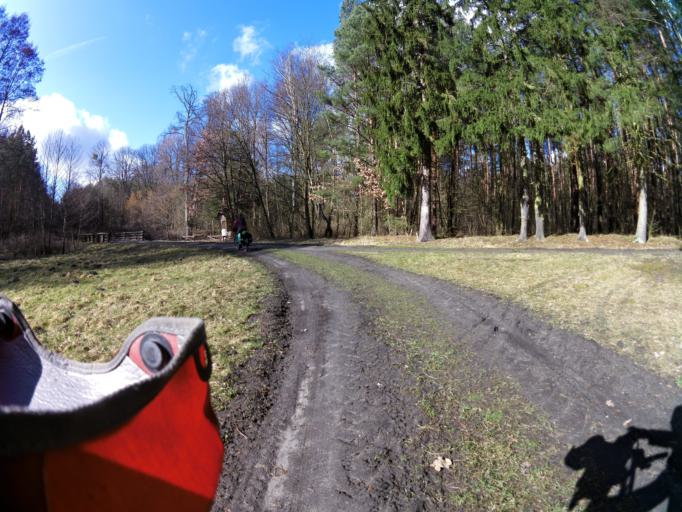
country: PL
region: West Pomeranian Voivodeship
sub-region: Powiat mysliborski
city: Debno
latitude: 52.7543
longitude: 14.7216
